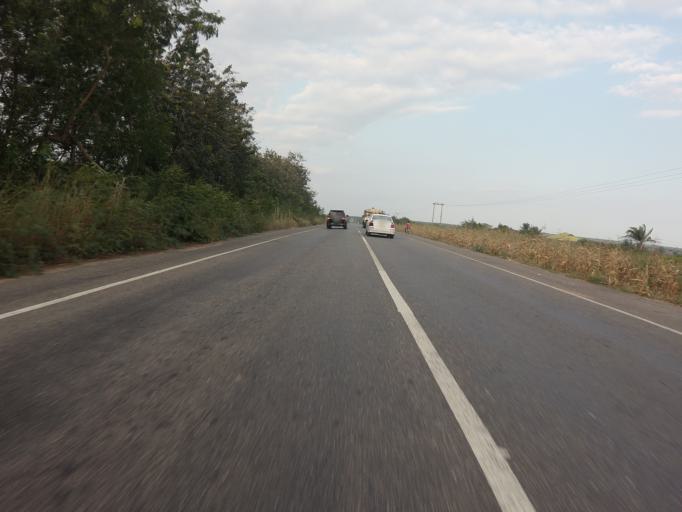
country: GH
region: Volta
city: Anloga
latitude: 6.0873
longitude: 0.5090
